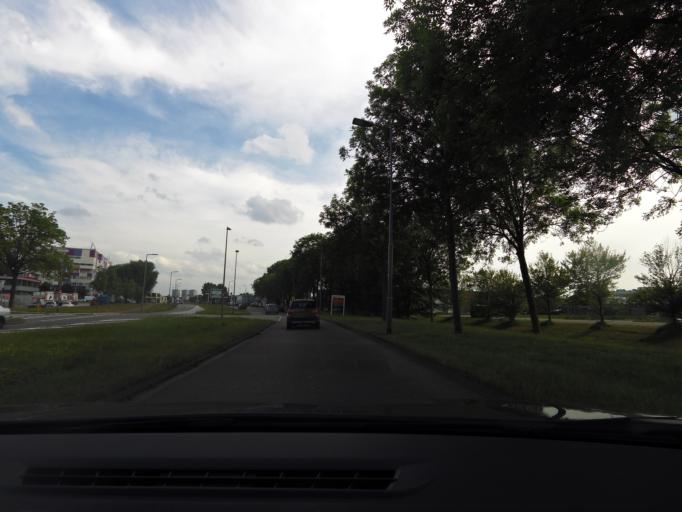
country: NL
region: South Holland
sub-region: Gemeente Schiedam
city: Schiedam
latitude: 51.9320
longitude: 4.4111
